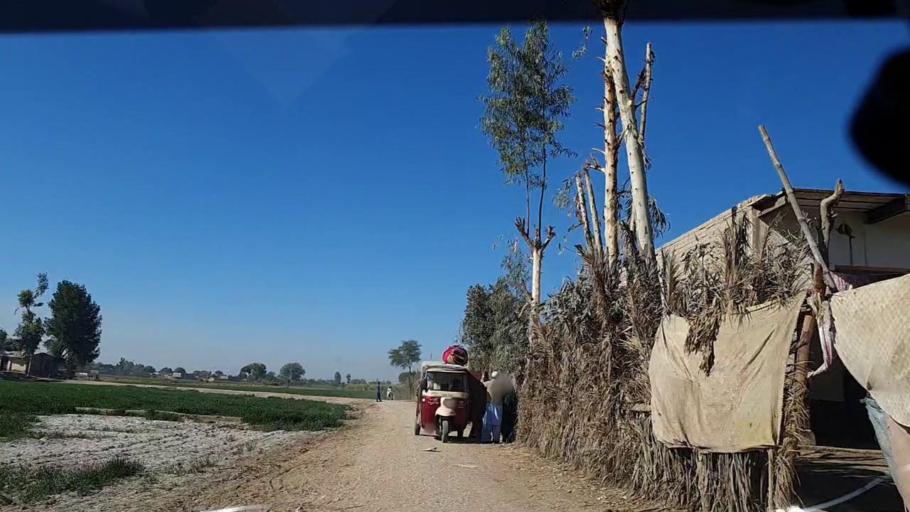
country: PK
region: Sindh
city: Ghotki
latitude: 27.9730
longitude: 69.3161
